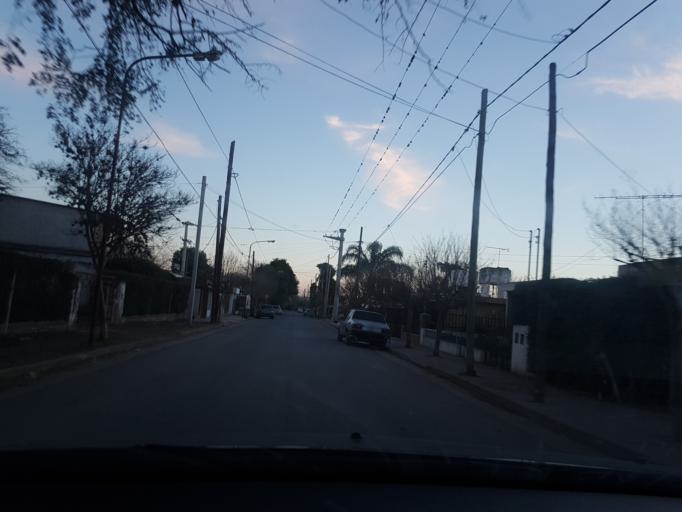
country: AR
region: Cordoba
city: Villa Allende
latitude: -31.2910
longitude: -64.2993
